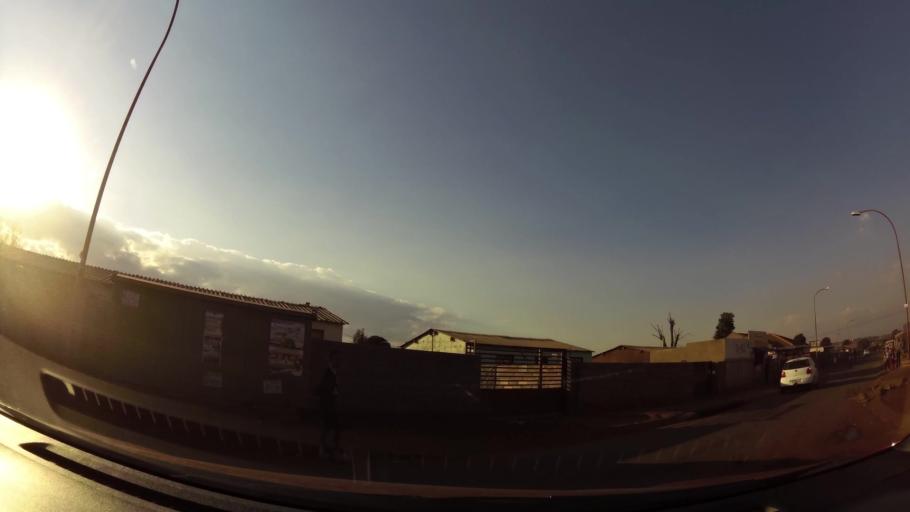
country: ZA
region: Gauteng
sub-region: City of Johannesburg Metropolitan Municipality
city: Soweto
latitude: -26.2264
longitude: 27.8571
